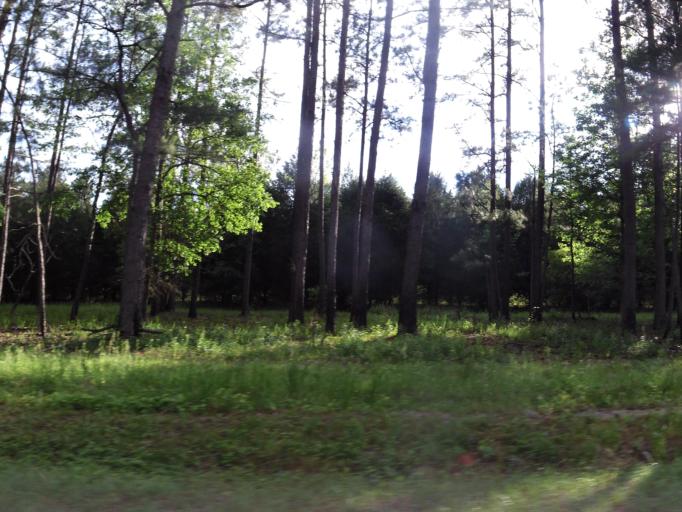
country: US
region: South Carolina
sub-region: Jasper County
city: Ridgeland
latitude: 32.5493
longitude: -81.1652
